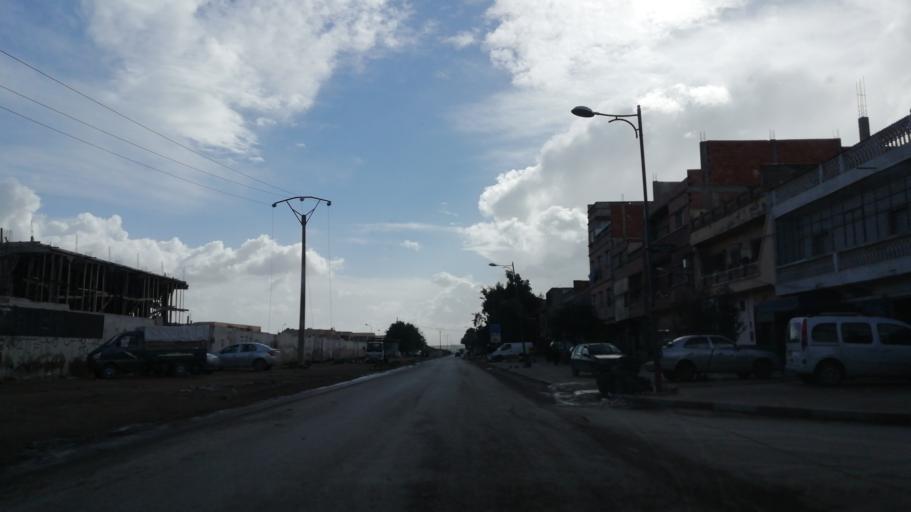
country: DZ
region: Oran
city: Sidi ech Chahmi
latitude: 35.6500
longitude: -0.5645
